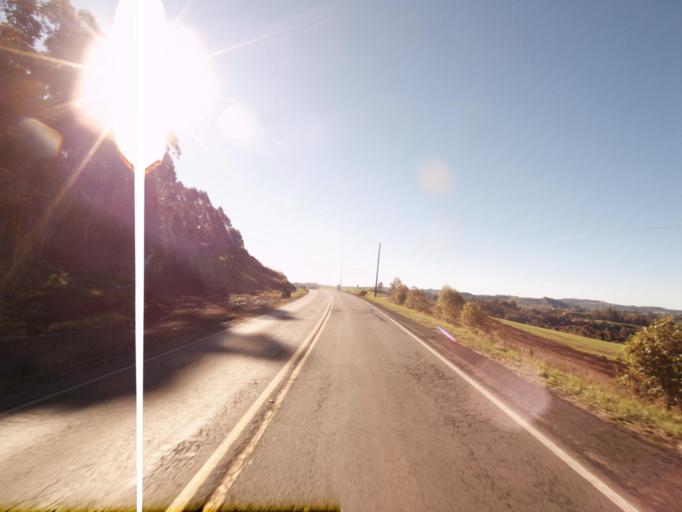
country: AR
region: Misiones
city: Bernardo de Irigoyen
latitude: -26.6237
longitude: -53.5161
